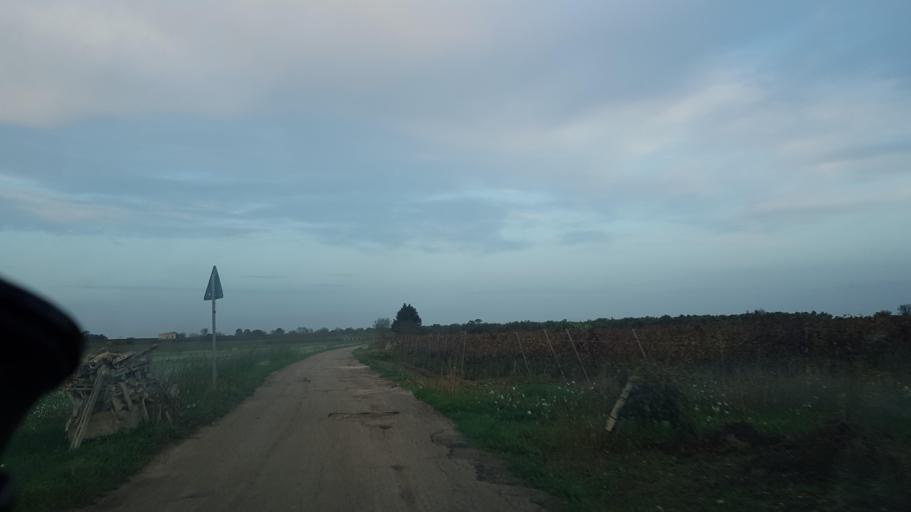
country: IT
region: Apulia
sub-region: Provincia di Brindisi
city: San Donaci
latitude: 40.4269
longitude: 17.9270
